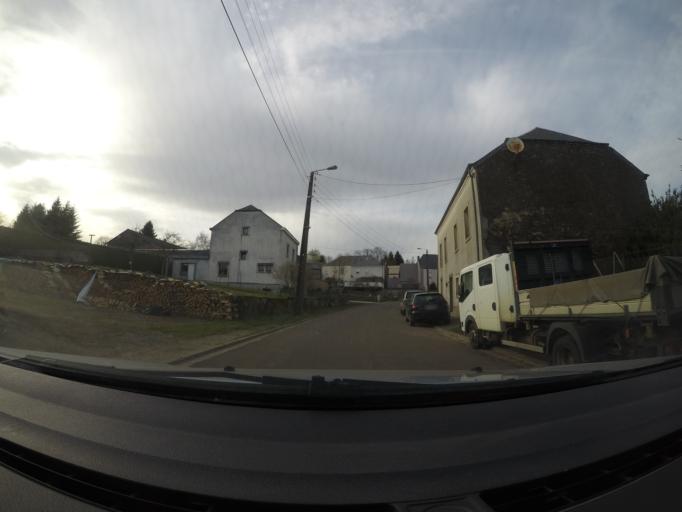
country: LU
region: Luxembourg
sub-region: Canton de Capellen
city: Clemency
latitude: 49.6084
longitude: 5.8465
